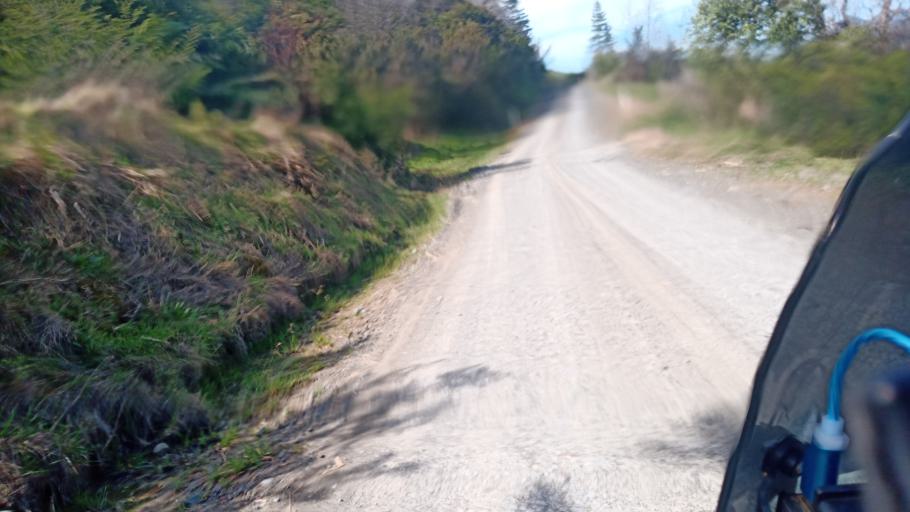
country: NZ
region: Gisborne
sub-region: Gisborne District
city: Gisborne
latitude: -37.8523
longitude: 178.0851
